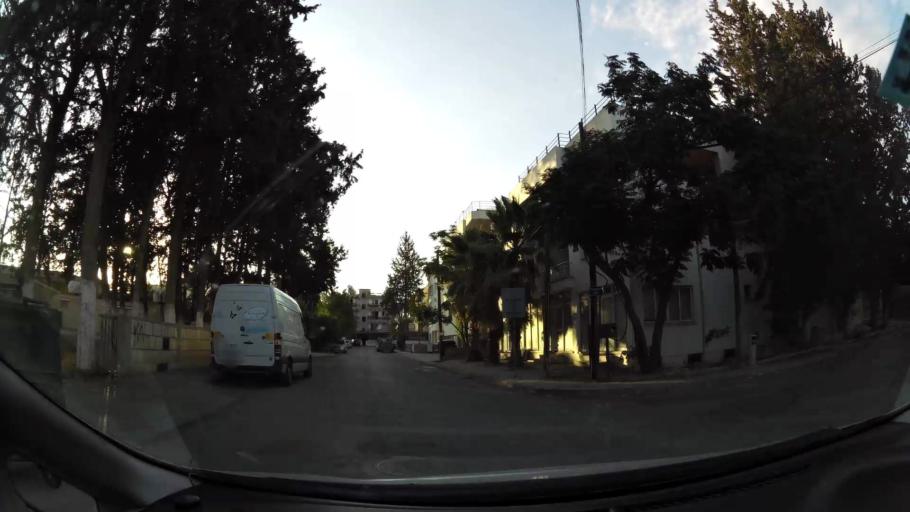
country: CY
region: Lefkosia
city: Nicosia
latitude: 35.1884
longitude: 33.3685
